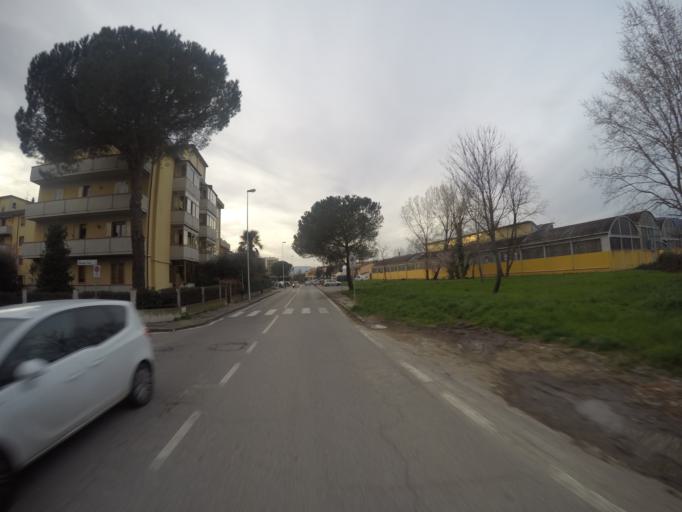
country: IT
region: Tuscany
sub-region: Provincia di Prato
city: Prato
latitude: 43.8888
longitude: 11.0604
